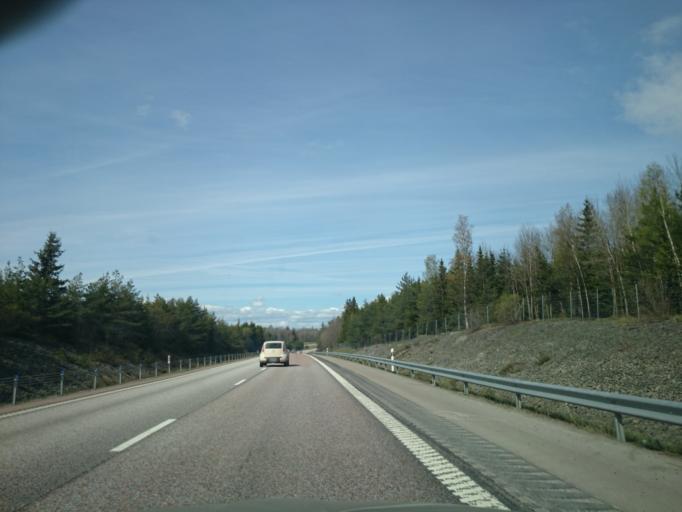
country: SE
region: Uppsala
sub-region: Uppsala Kommun
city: Alsike
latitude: 59.7741
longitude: 17.7852
